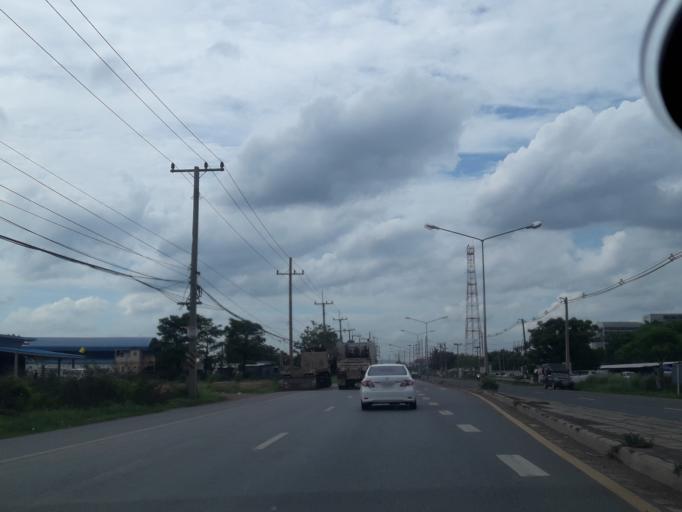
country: TH
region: Sara Buri
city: Kaeng Khoi
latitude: 14.5637
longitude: 101.0072
